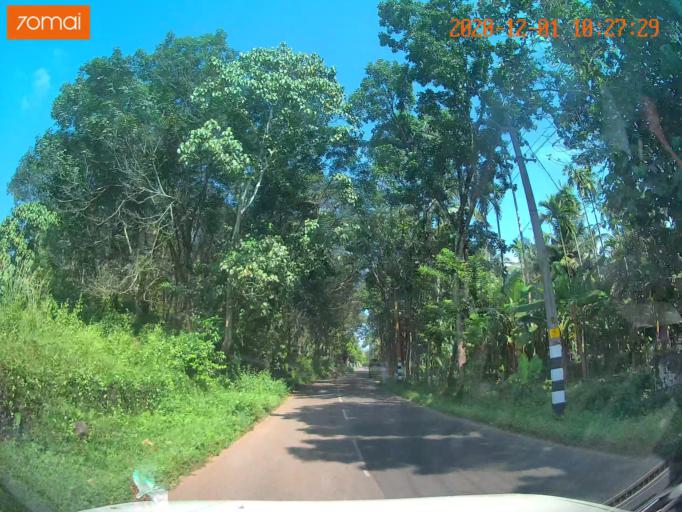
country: IN
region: Kerala
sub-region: Ernakulam
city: Ramamangalam
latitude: 9.9291
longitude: 76.5228
